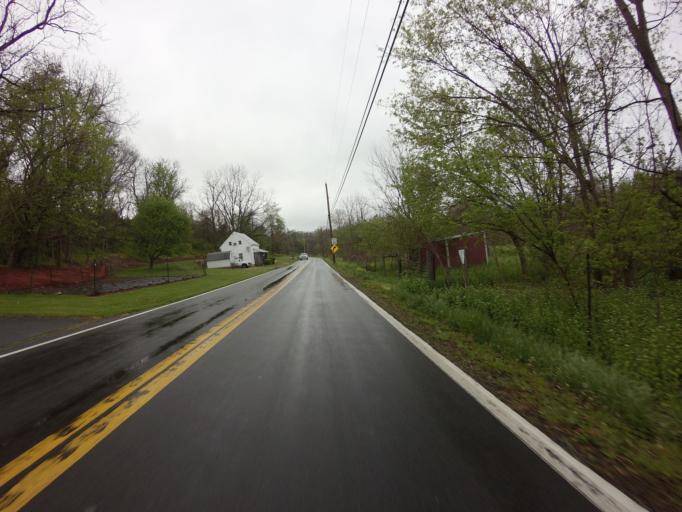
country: US
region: Maryland
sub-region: Frederick County
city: Myersville
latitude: 39.4858
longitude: -77.5338
